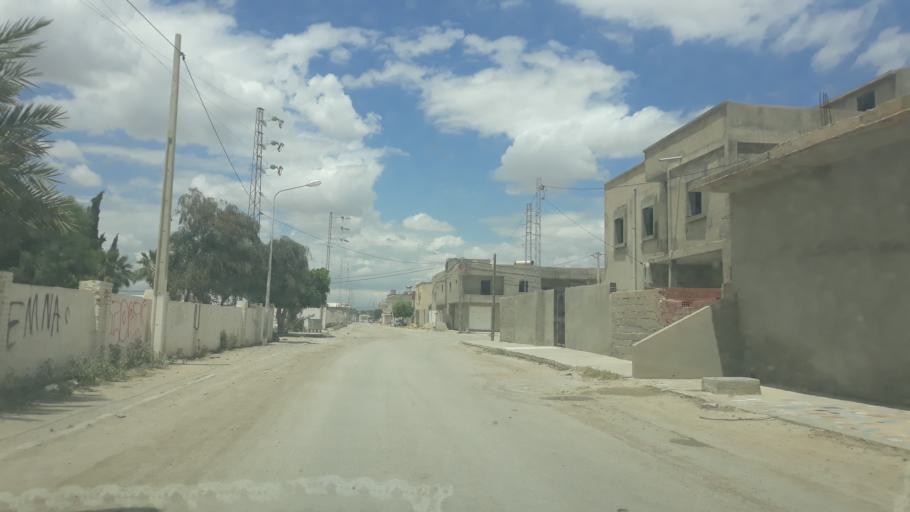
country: TN
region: Al Qayrawan
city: Kairouan
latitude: 35.6190
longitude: 9.9233
